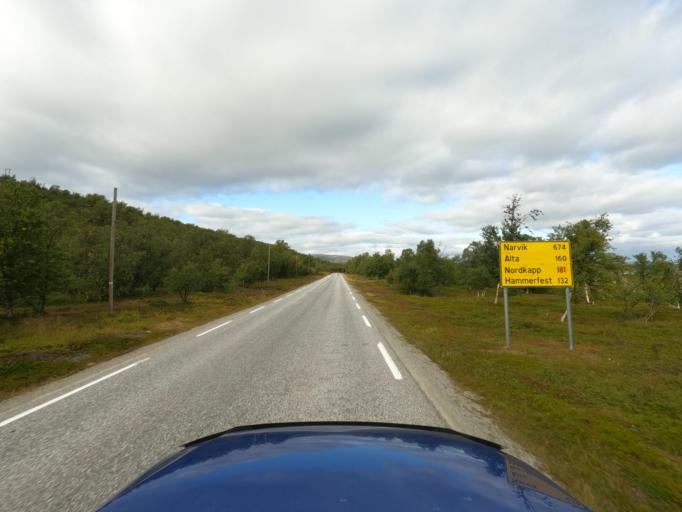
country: NO
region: Finnmark Fylke
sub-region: Porsanger
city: Lakselv
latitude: 70.1427
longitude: 24.9085
